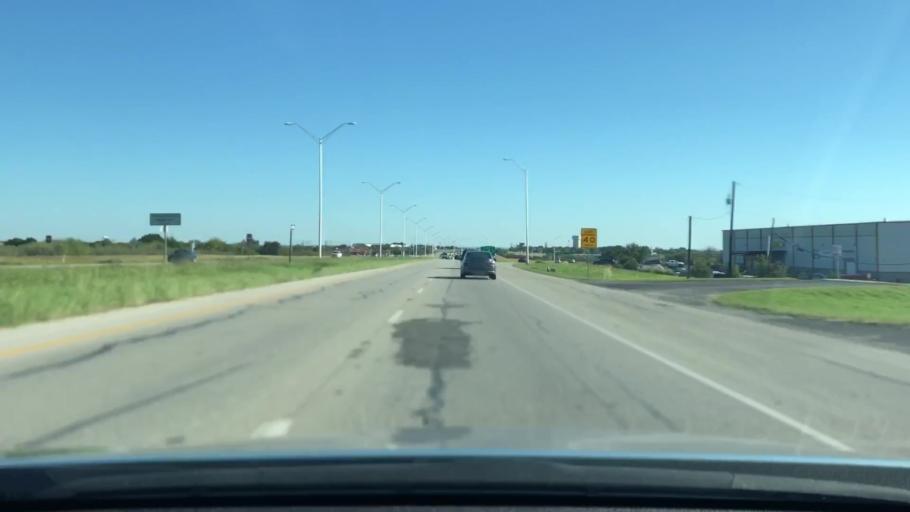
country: US
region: Texas
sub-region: Bexar County
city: Universal City
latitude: 29.5397
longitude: -98.3063
